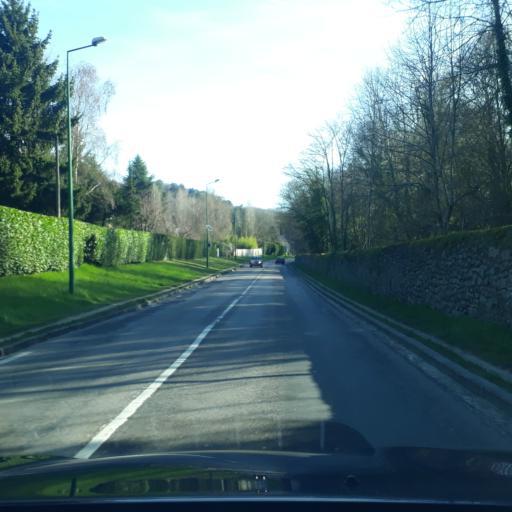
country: FR
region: Ile-de-France
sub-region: Departement de l'Essonne
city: La Ferte-Alais
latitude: 48.4855
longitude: 2.3392
